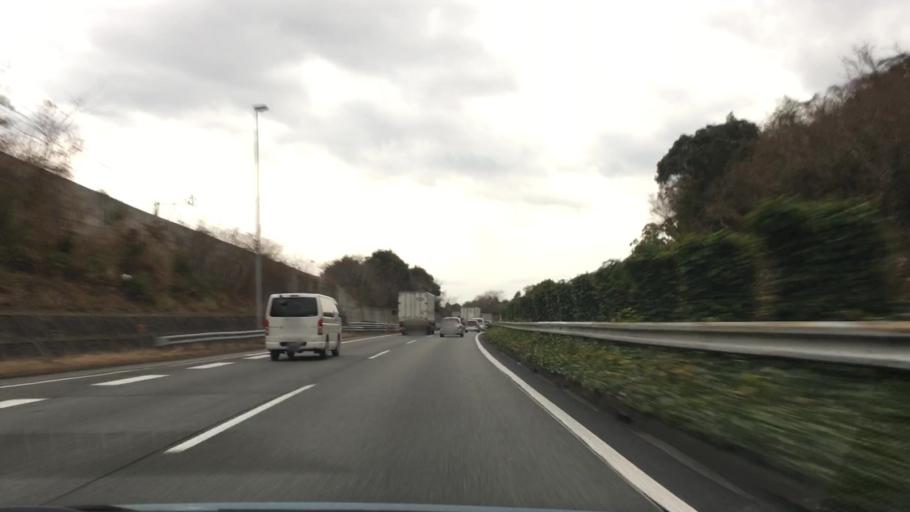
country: JP
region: Shizuoka
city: Fujinomiya
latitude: 35.1546
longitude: 138.6174
